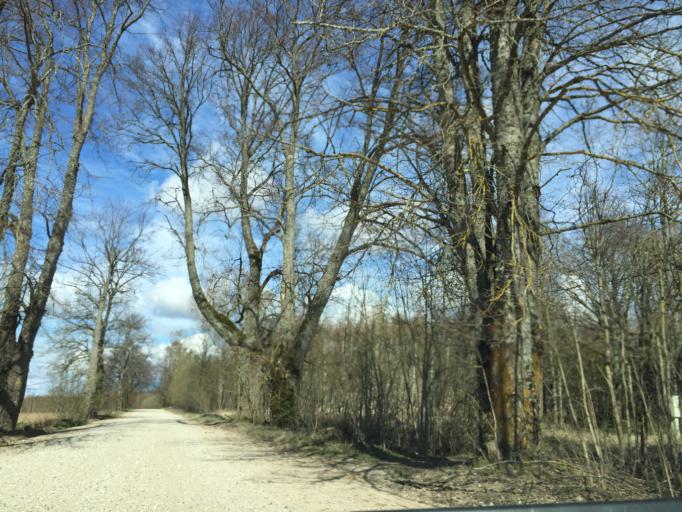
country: LV
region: Limbazu Rajons
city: Limbazi
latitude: 57.5722
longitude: 24.5936
